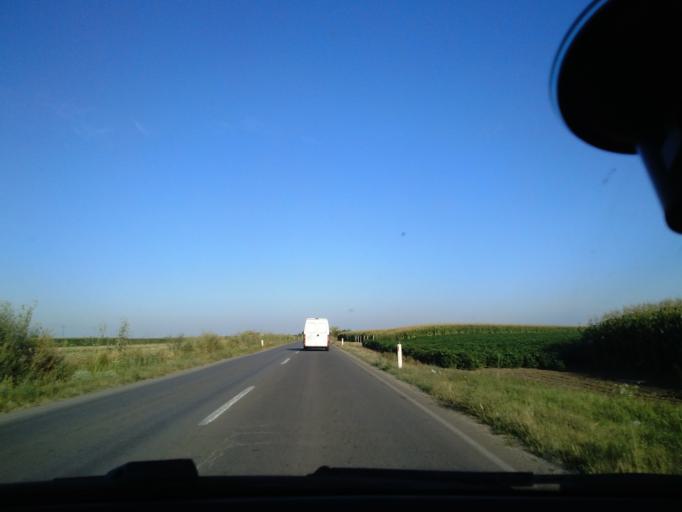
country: RS
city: Obrovac
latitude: 45.4070
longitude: 19.4224
